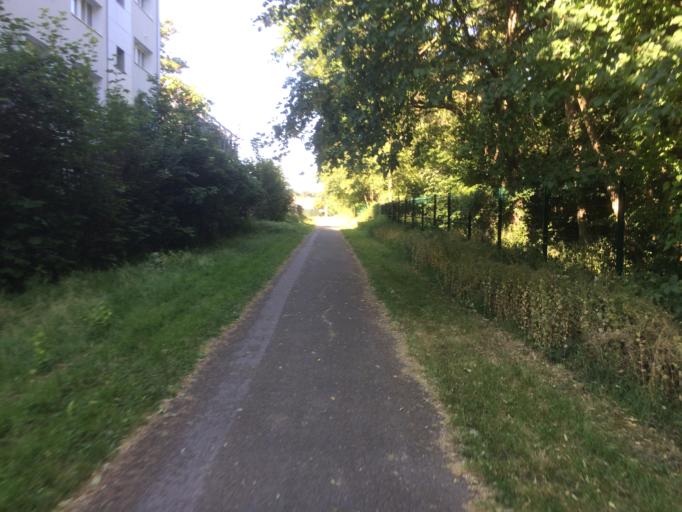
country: FR
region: Ile-de-France
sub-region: Departement du Val-de-Marne
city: Boissy-Saint-Leger
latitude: 48.7494
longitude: 2.5179
